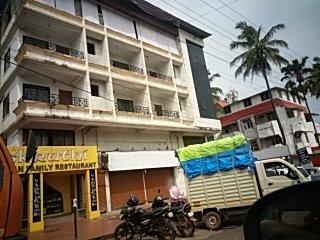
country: IN
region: Goa
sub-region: North Goa
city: Serula
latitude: 15.5300
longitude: 73.8254
